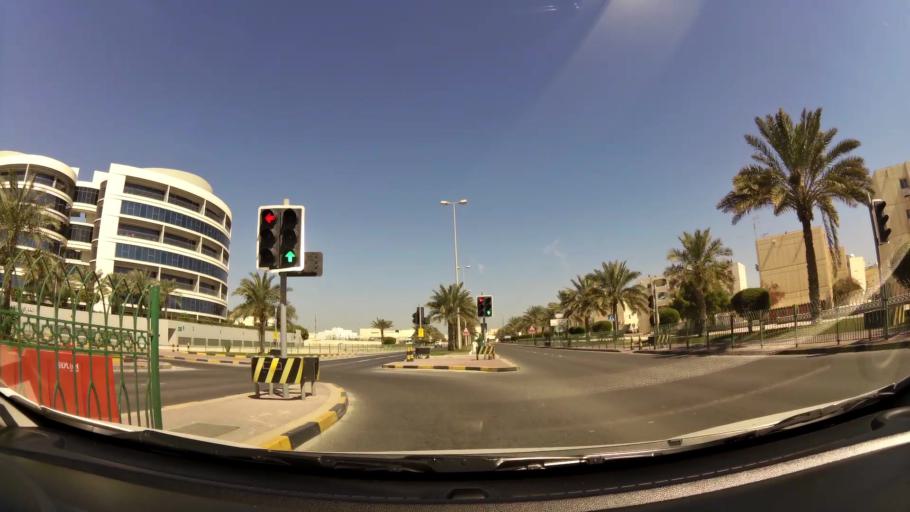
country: BH
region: Muharraq
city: Al Muharraq
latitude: 26.2639
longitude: 50.6033
